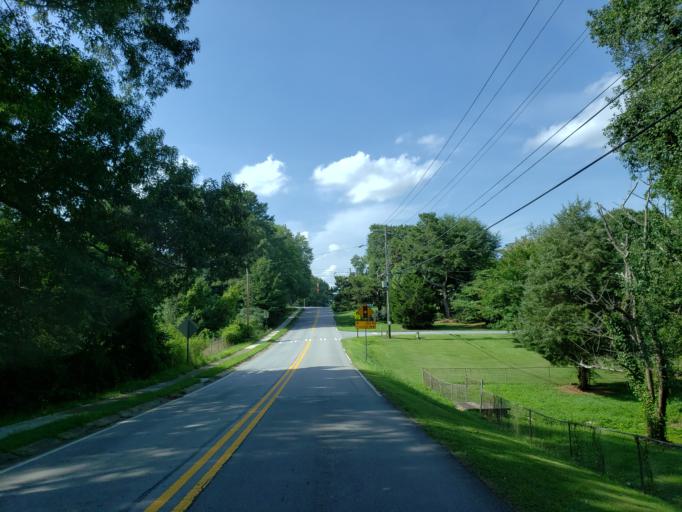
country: US
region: Georgia
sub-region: Cobb County
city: Mableton
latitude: 33.8630
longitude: -84.5689
